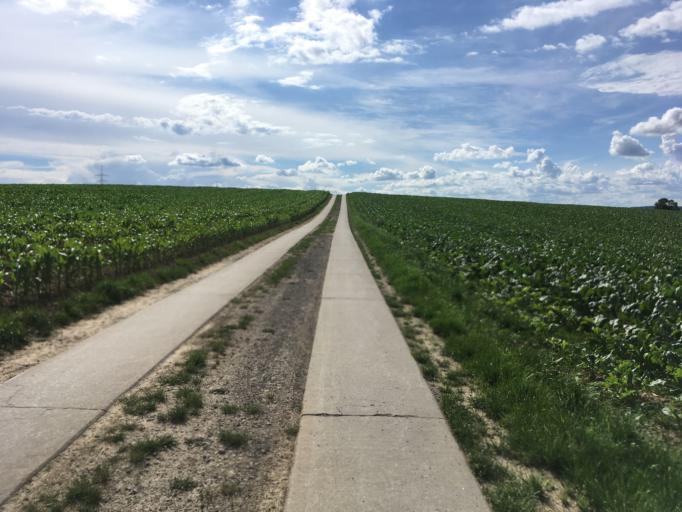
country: DE
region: Baden-Wuerttemberg
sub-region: Regierungsbezirk Stuttgart
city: Oberriexingen
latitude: 48.9400
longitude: 9.0022
